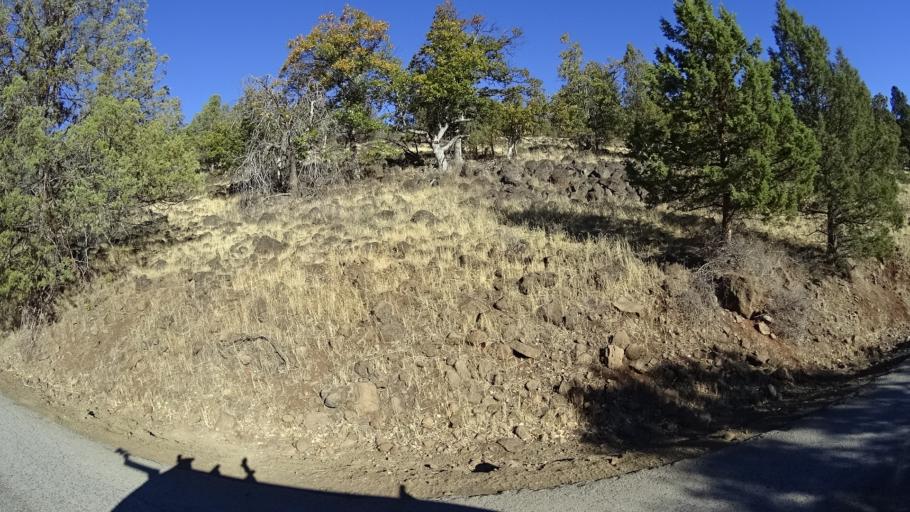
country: US
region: California
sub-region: Siskiyou County
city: Montague
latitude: 41.9752
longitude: -122.4040
